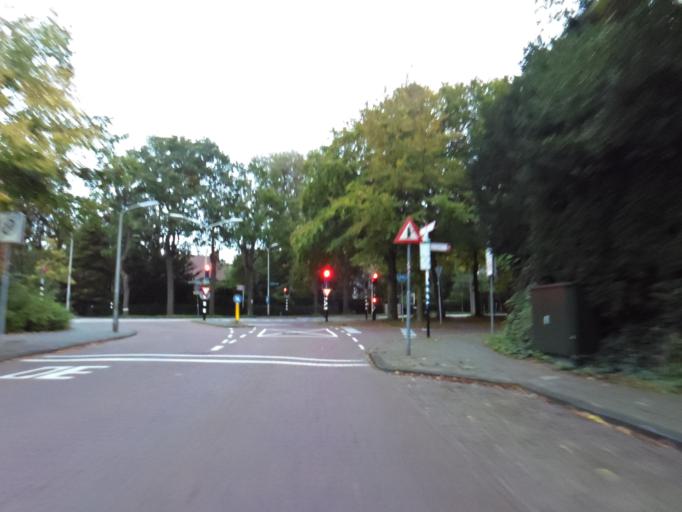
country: NL
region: South Holland
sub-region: Gemeente Wassenaar
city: Wassenaar
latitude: 52.1235
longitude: 4.3634
